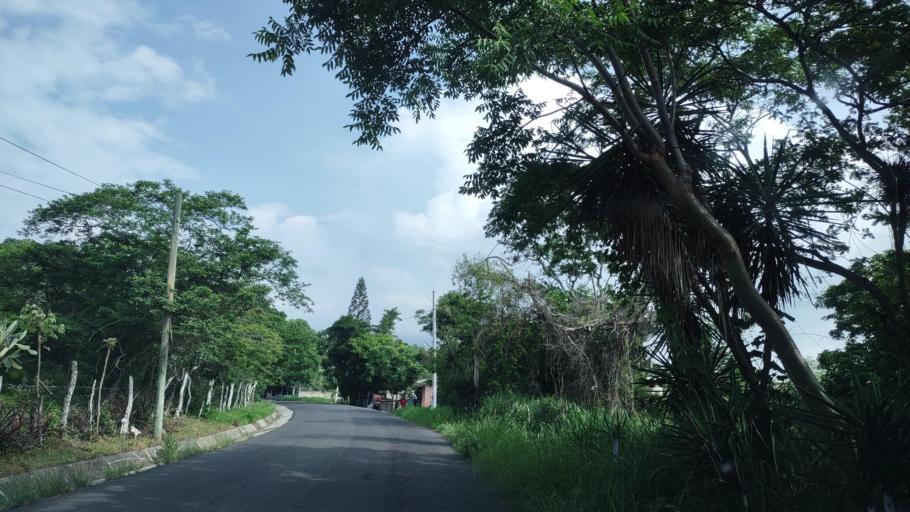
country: MX
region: Veracruz
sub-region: Coatepec
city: Bella Esperanza
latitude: 19.4517
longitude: -96.8283
